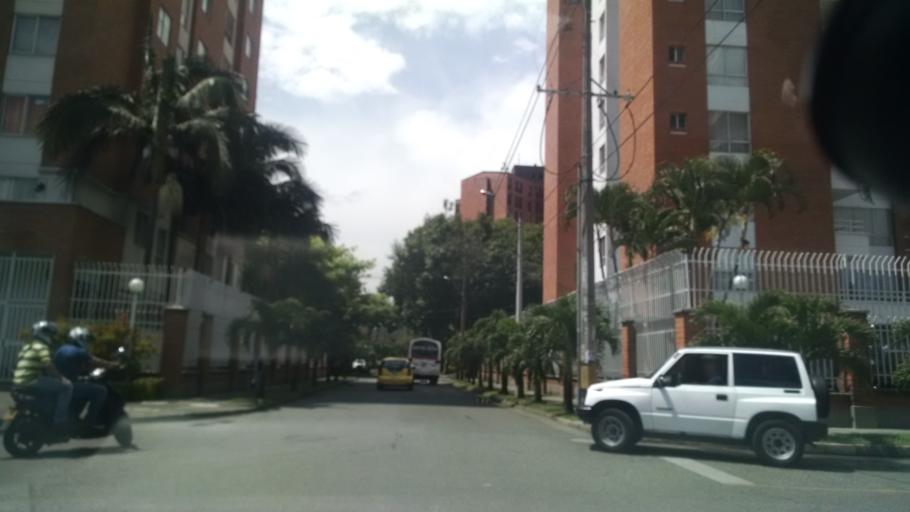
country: CO
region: Antioquia
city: Medellin
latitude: 6.2547
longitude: -75.5840
